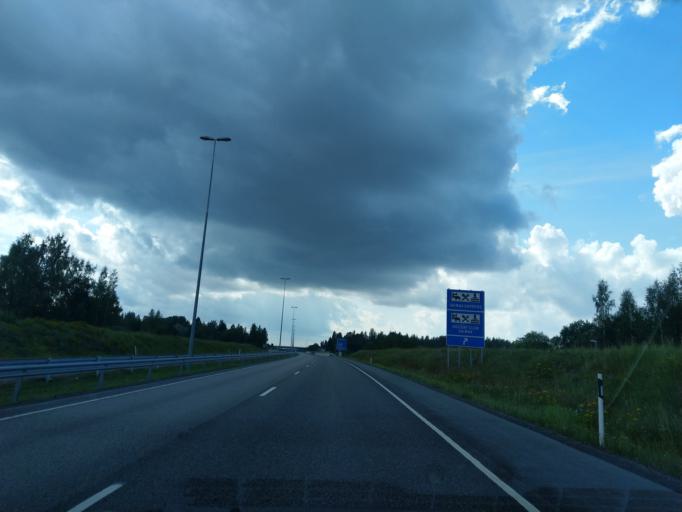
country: FI
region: South Karelia
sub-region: Imatra
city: Imatra
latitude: 61.1765
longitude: 28.7106
